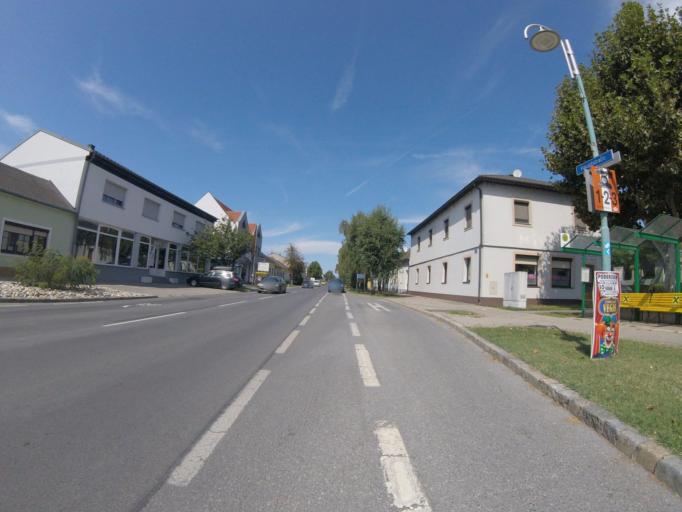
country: AT
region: Burgenland
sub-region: Politischer Bezirk Neusiedl am See
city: Podersdorf am See
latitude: 47.8526
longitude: 16.8393
